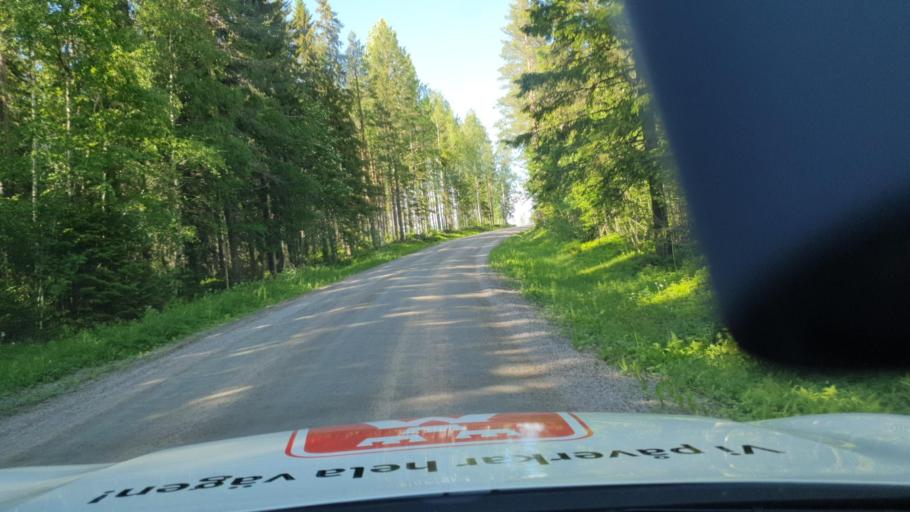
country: SE
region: Vaesterbotten
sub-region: Vannas Kommun
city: Vaennaes
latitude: 63.7885
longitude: 19.6239
